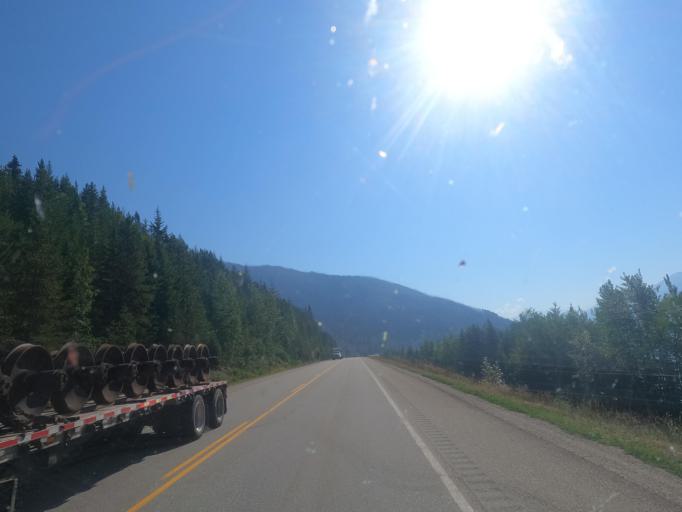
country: CA
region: Alberta
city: Jasper Park Lodge
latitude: 52.9542
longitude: -118.8809
